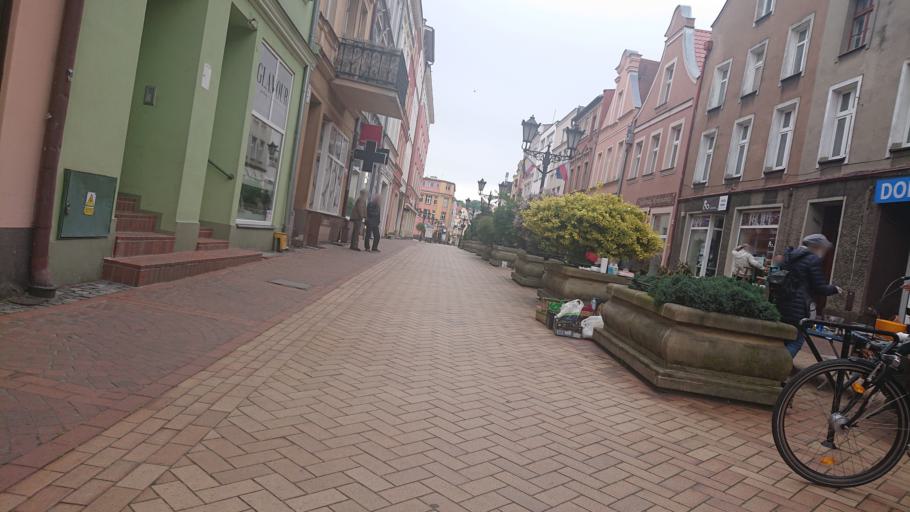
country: PL
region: Pomeranian Voivodeship
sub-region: Powiat chojnicki
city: Chojnice
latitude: 53.6954
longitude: 17.5597
